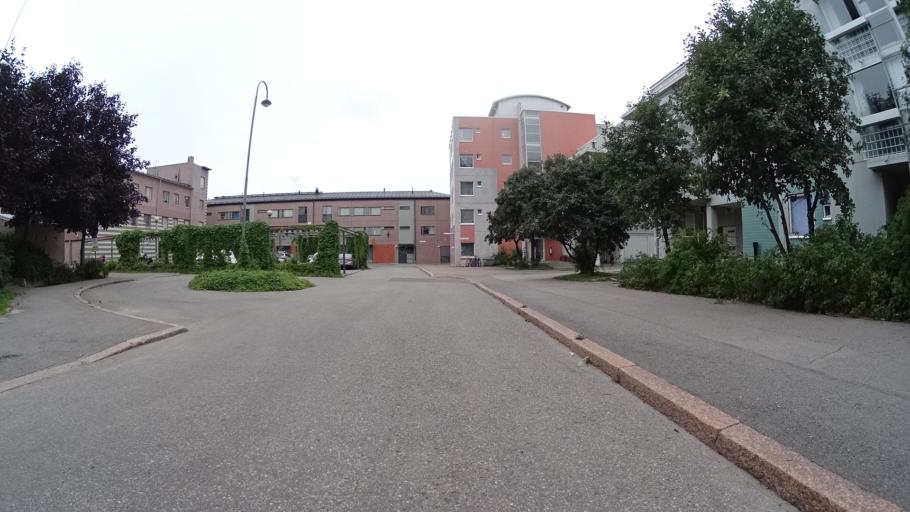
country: FI
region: Uusimaa
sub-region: Helsinki
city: Helsinki
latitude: 60.1998
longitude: 24.8963
